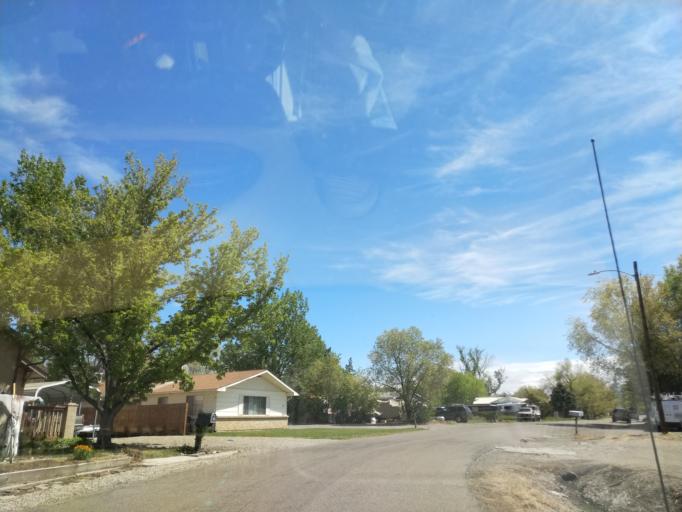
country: US
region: Colorado
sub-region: Mesa County
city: Grand Junction
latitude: 39.0800
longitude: -108.5755
